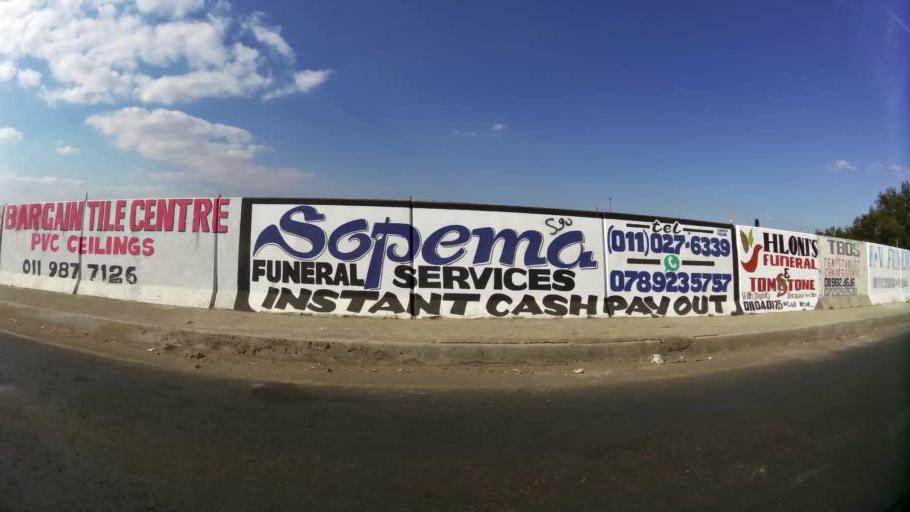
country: ZA
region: Gauteng
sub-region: City of Johannesburg Metropolitan Municipality
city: Soweto
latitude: -26.2687
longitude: 27.8900
